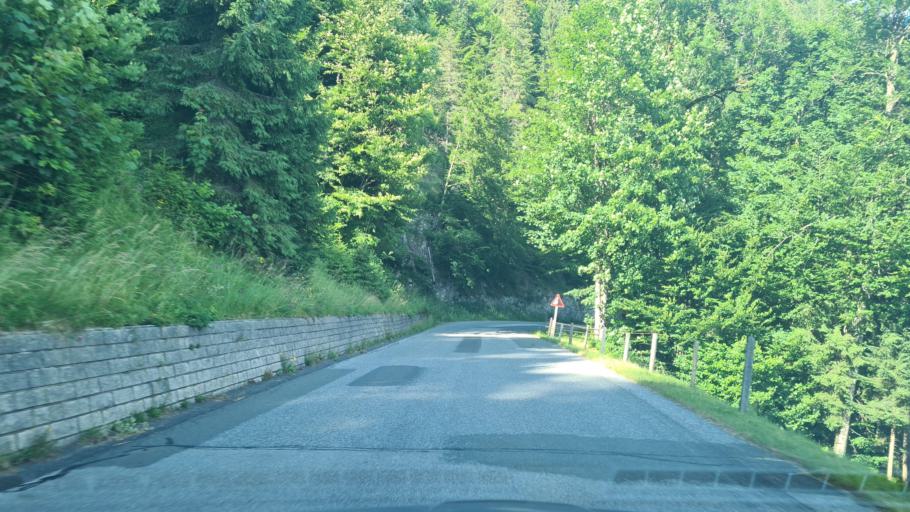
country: AT
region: Salzburg
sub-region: Politischer Bezirk Zell am See
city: Unken
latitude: 47.6521
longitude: 12.6850
